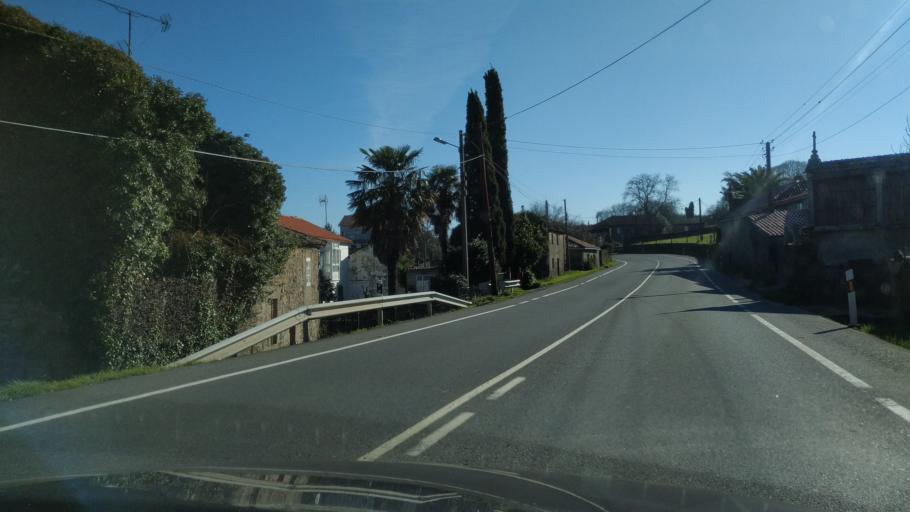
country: ES
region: Galicia
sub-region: Provincia de Pontevedra
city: Silleda
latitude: 42.7235
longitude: -8.2951
